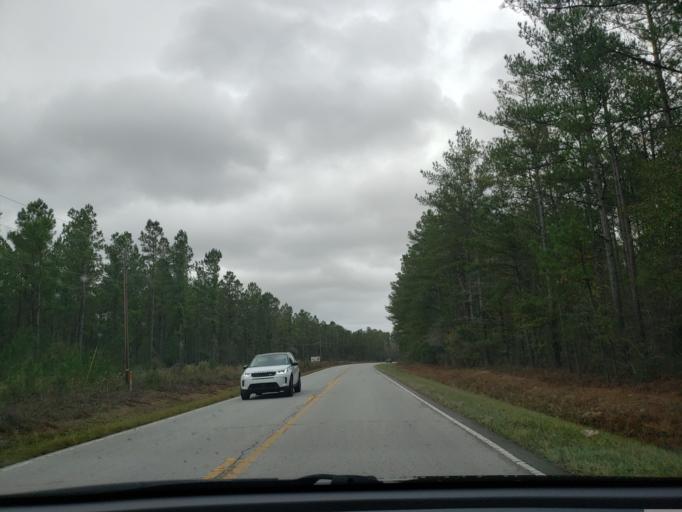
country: US
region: North Carolina
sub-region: Onslow County
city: Half Moon
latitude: 34.7316
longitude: -77.5933
